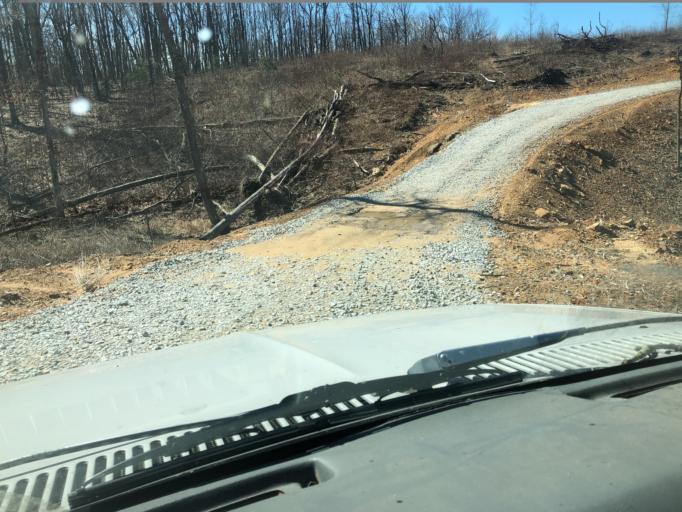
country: US
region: Tennessee
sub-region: Roane County
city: Rockwood
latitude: 35.9739
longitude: -84.7510
